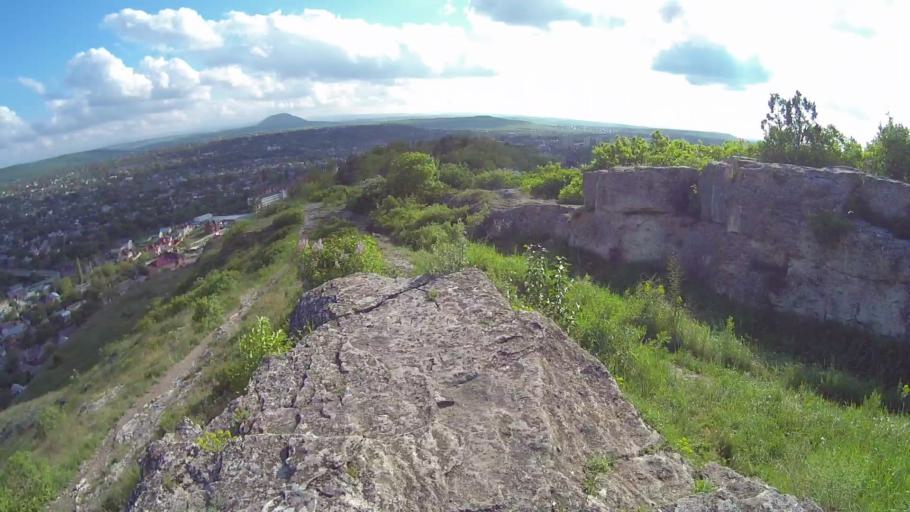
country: RU
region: Stavropol'skiy
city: Goryachevodskiy
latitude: 44.0376
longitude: 43.0873
